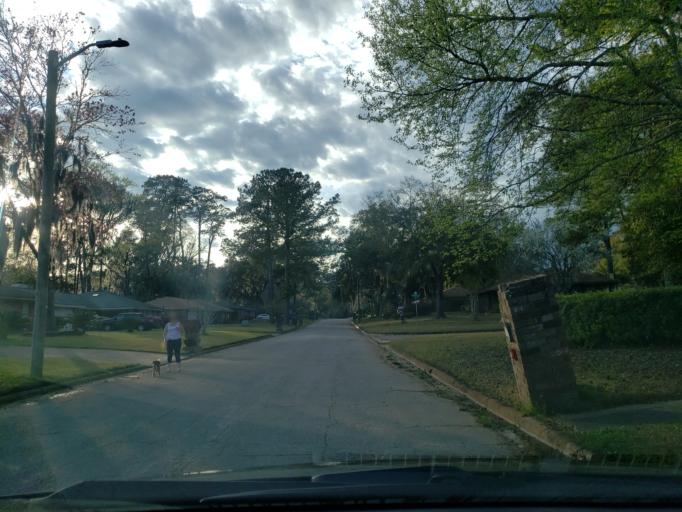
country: US
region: Georgia
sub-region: Chatham County
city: Montgomery
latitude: 31.9945
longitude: -81.1378
